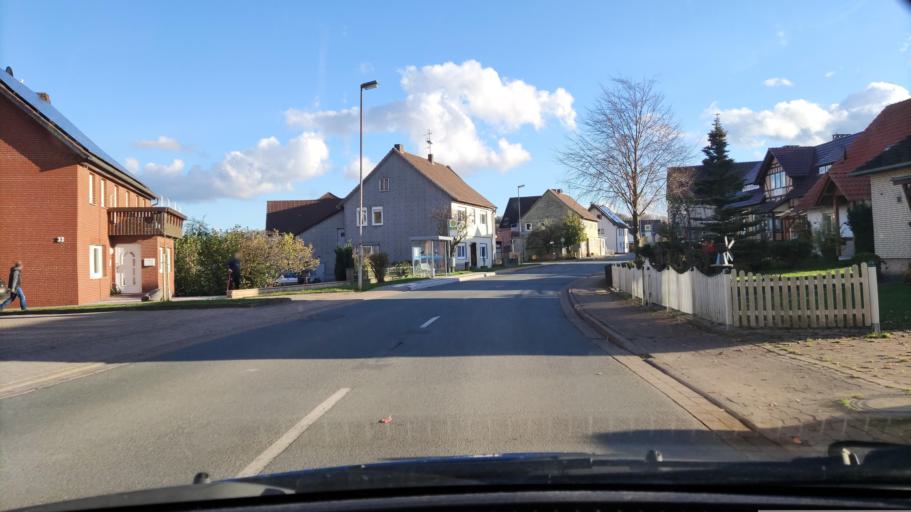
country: DE
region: Lower Saxony
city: Heinade
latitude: 51.8377
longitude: 9.6347
